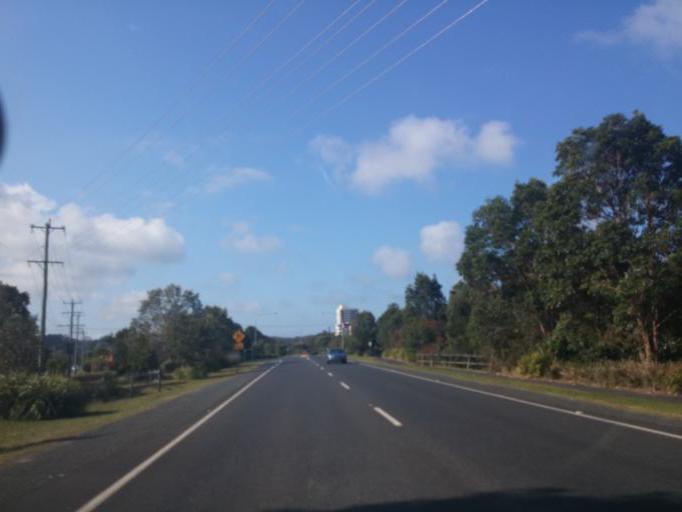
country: AU
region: New South Wales
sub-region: Coffs Harbour
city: Coffs Harbour
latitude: -30.2887
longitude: 153.1355
